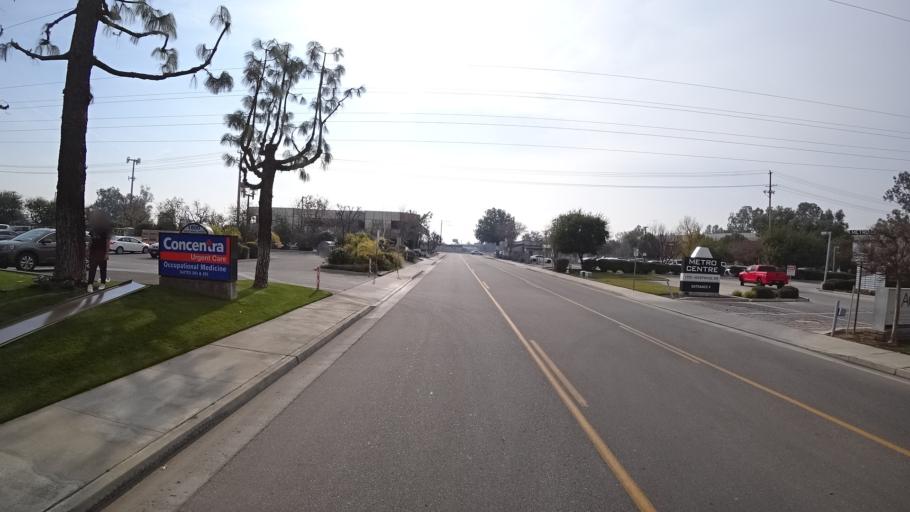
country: US
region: California
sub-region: Kern County
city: Bakersfield
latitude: 35.3751
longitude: -119.0425
